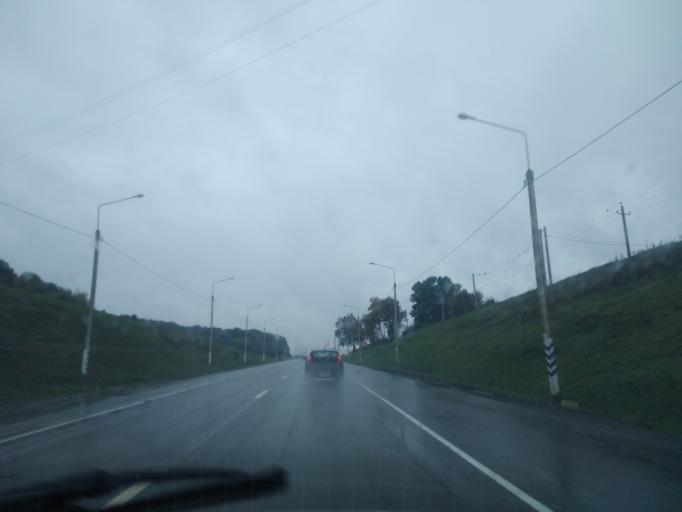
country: RU
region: Tula
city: Shchekino
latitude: 54.0068
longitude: 37.4767
